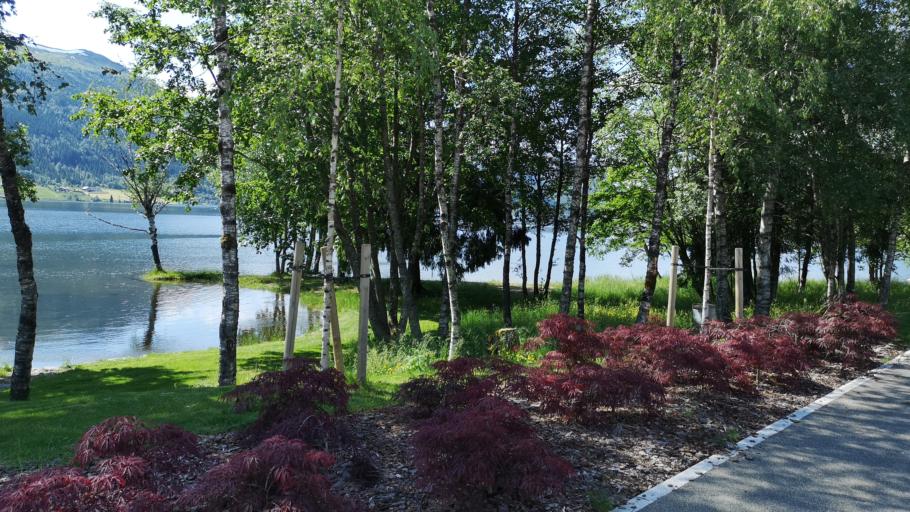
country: NO
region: Sogn og Fjordane
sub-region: Gloppen
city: Sandane
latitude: 61.5107
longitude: 6.1558
